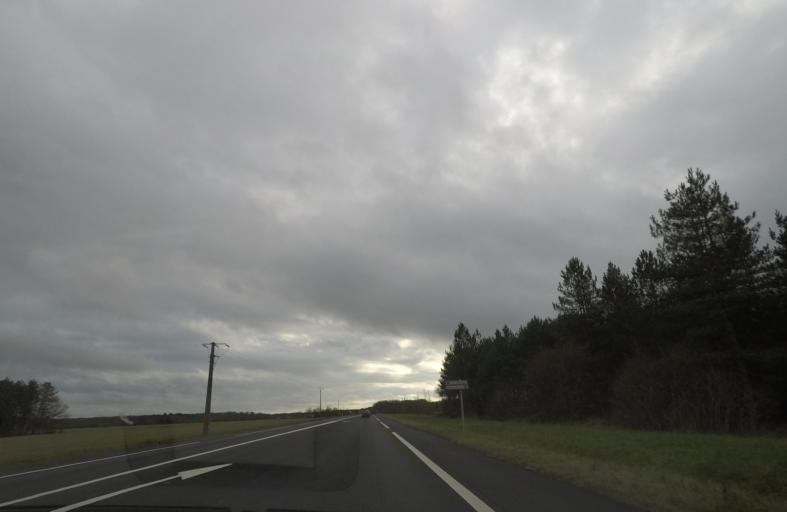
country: FR
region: Centre
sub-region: Departement du Loir-et-Cher
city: Soings-en-Sologne
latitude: 47.4491
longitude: 1.5362
